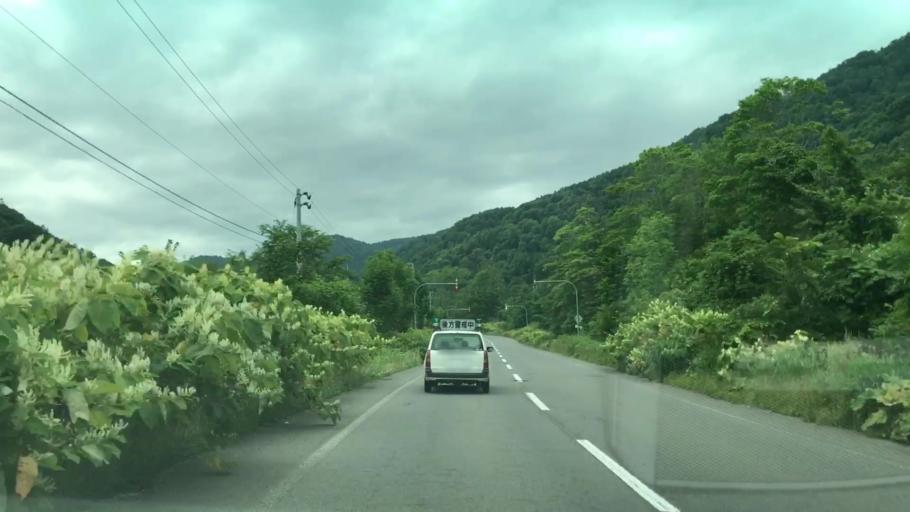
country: JP
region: Hokkaido
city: Yoichi
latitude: 43.0254
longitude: 140.8665
